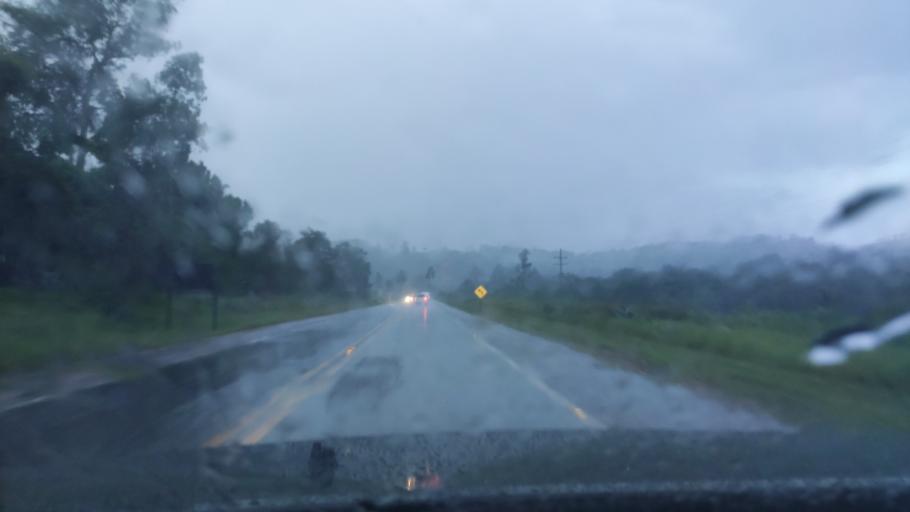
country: BR
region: Sao Paulo
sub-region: Braganca Paulista
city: Braganca Paulista
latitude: -22.7964
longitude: -46.5549
